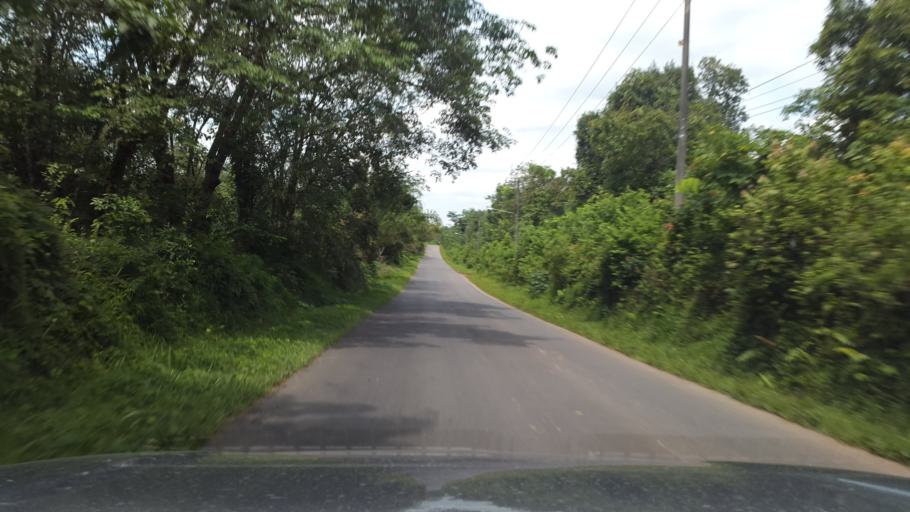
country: ID
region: South Sumatra
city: Gunungmegang Dalam
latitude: -3.3578
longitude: 103.9310
